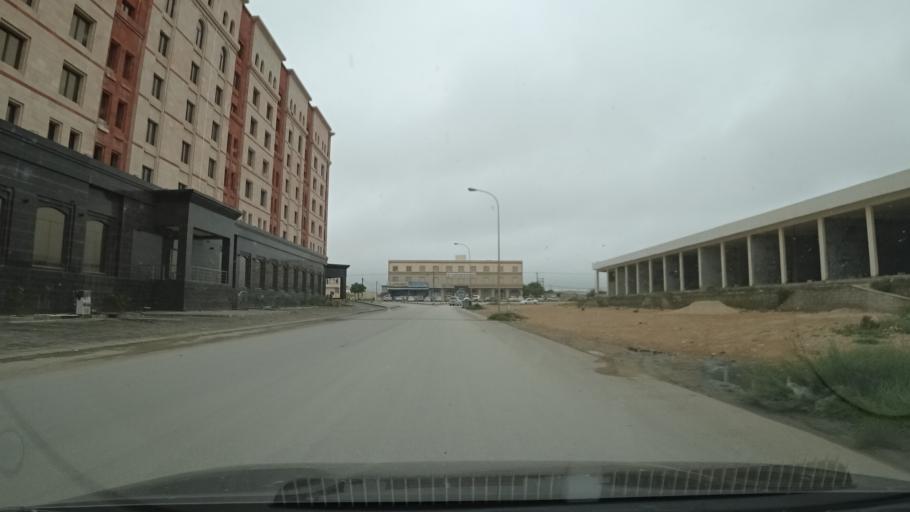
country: OM
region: Zufar
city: Salalah
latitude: 17.0221
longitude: 54.0399
